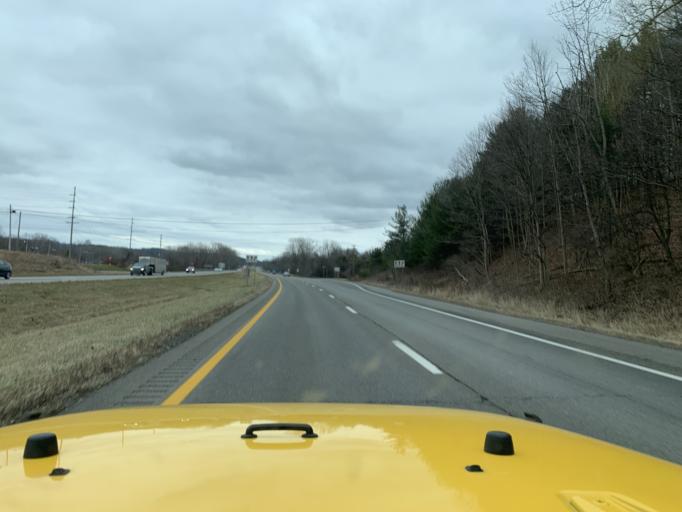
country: US
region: Ohio
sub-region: Licking County
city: Granville
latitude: 40.0570
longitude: -82.5120
